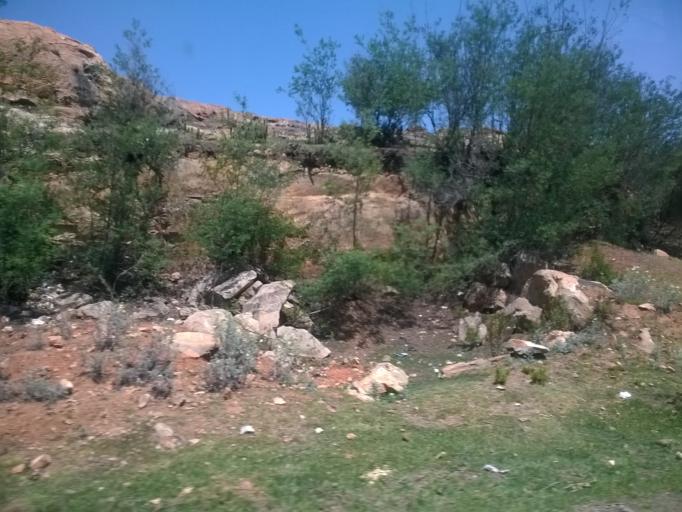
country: LS
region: Berea
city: Teyateyaneng
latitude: -29.1141
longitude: 27.8263
